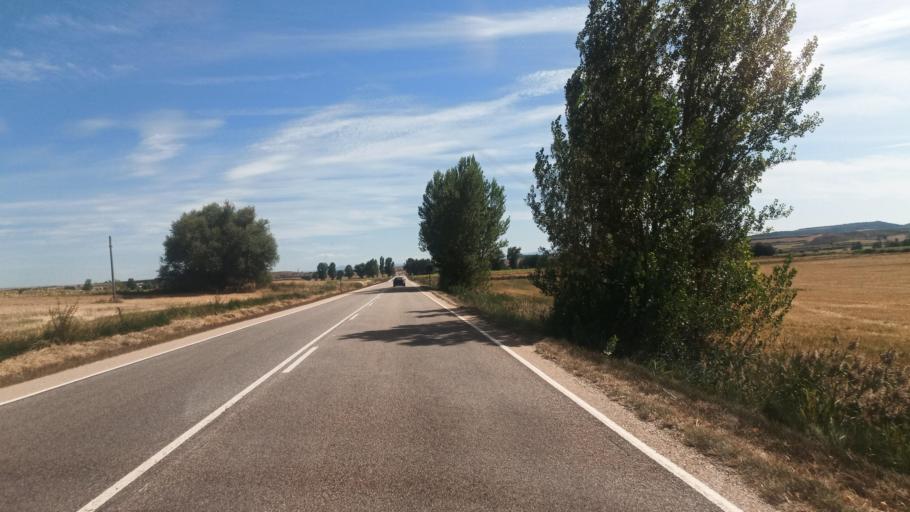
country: ES
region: Castille and Leon
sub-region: Provincia de Burgos
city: Quintanabureba
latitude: 42.6044
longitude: -3.3510
